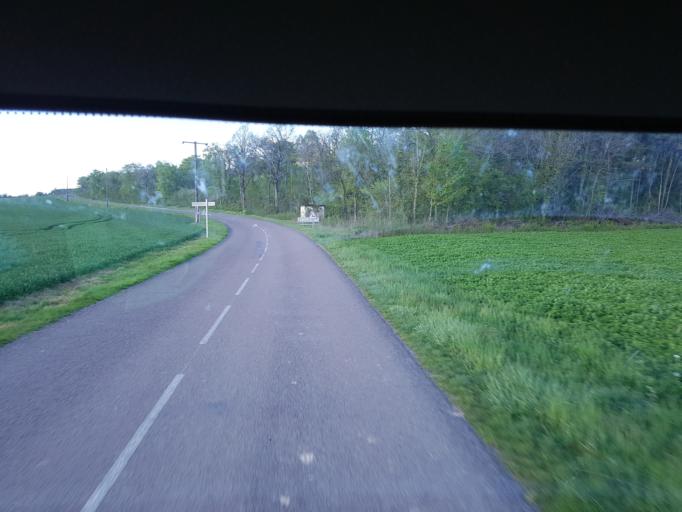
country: FR
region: Champagne-Ardenne
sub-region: Departement de l'Aube
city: Aix-en-Othe
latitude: 48.3086
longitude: 3.6359
